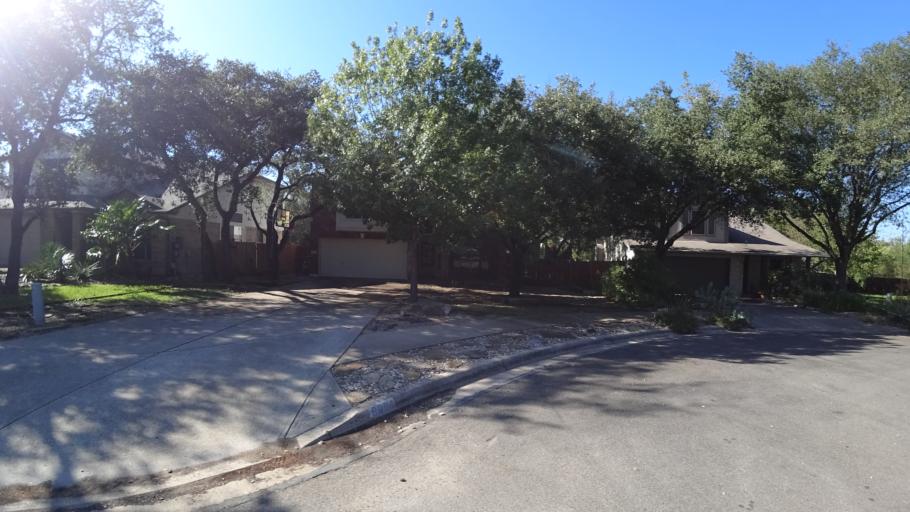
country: US
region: Texas
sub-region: Travis County
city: Shady Hollow
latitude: 30.2016
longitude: -97.8551
